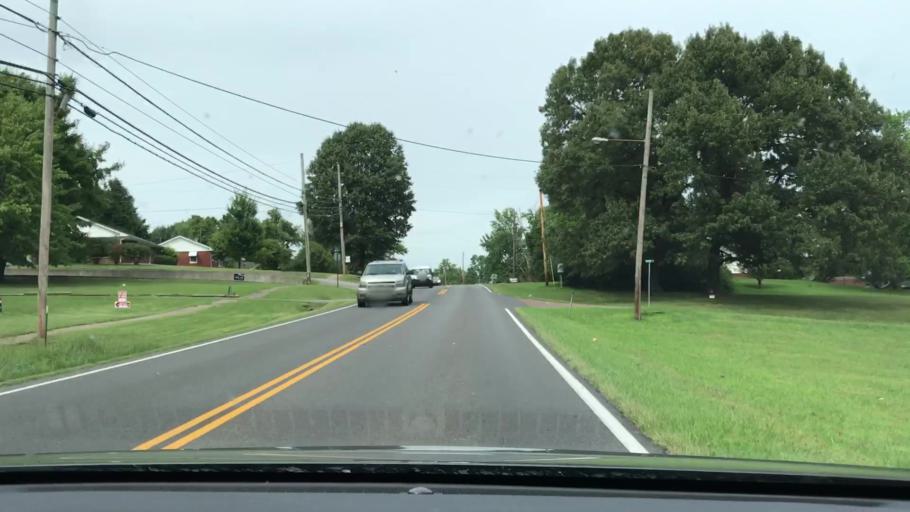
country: US
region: Kentucky
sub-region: Marshall County
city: Benton
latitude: 36.8404
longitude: -88.3502
